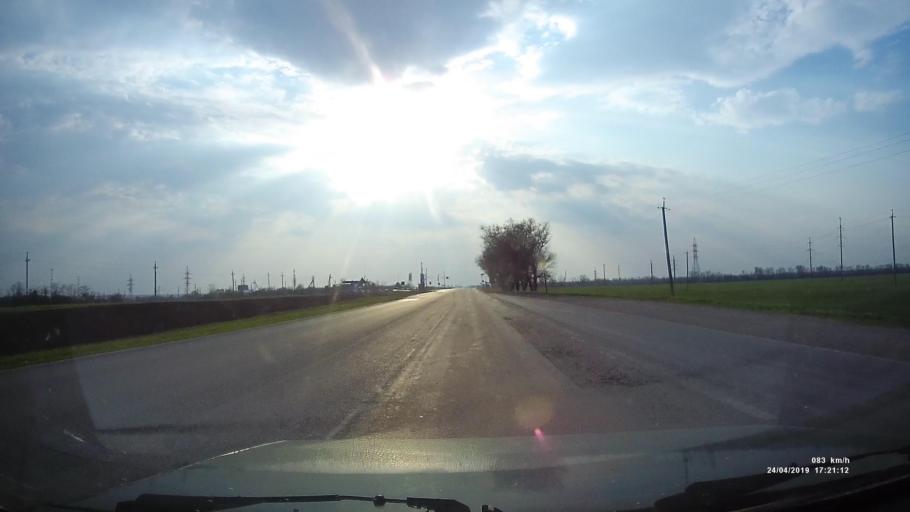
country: RU
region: Rostov
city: Gigant
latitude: 46.5182
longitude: 41.3361
